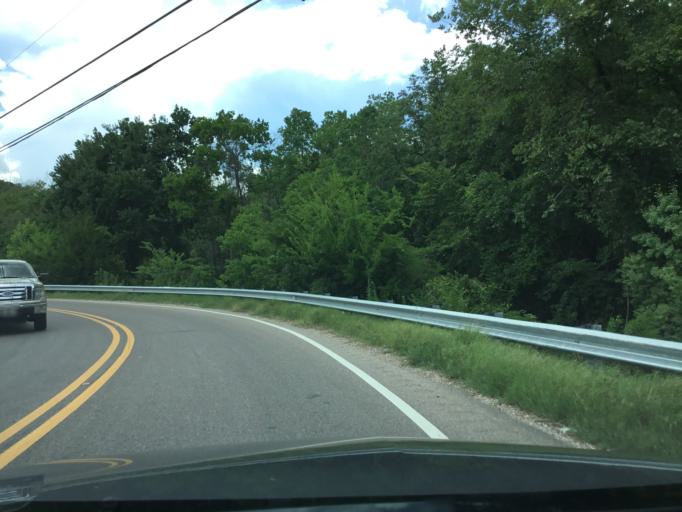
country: US
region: Alabama
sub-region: Montgomery County
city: Pike Road
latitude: 32.3683
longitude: -86.1023
